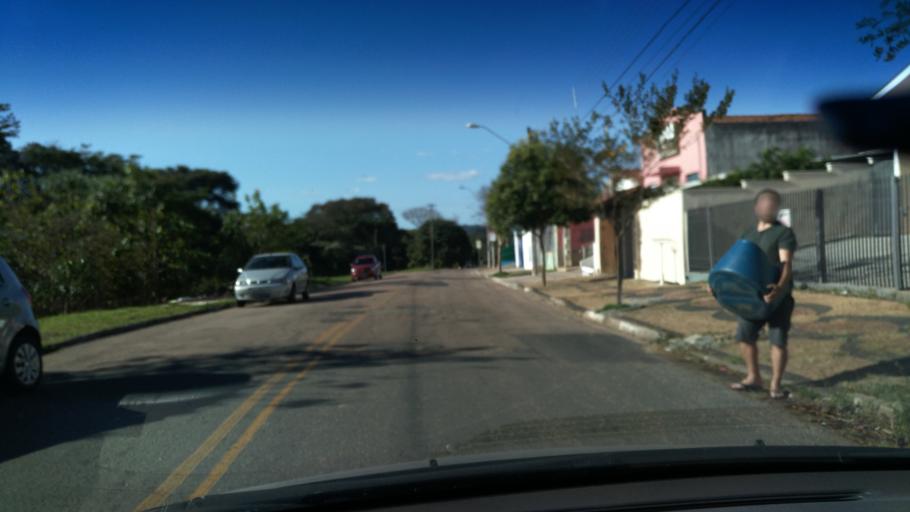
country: BR
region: Sao Paulo
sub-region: Valinhos
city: Valinhos
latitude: -22.9632
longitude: -46.9921
